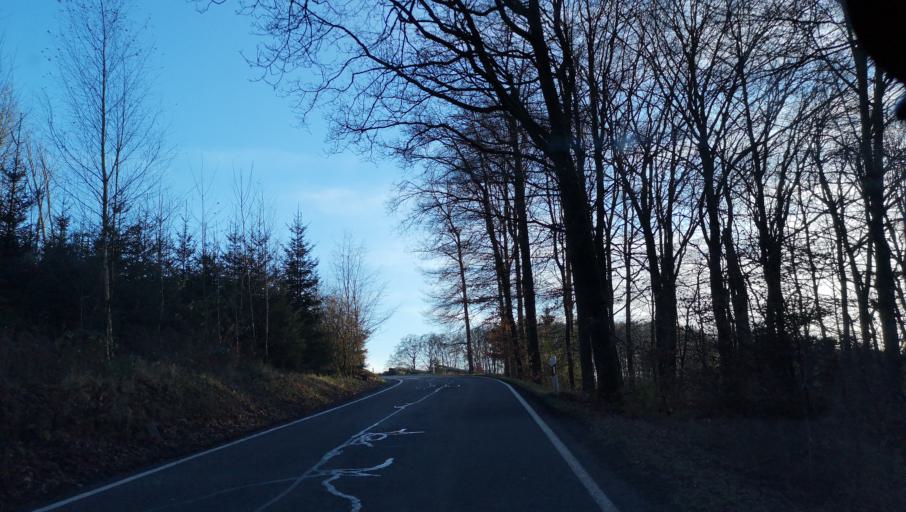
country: DE
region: North Rhine-Westphalia
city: Radevormwald
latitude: 51.1855
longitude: 7.3904
